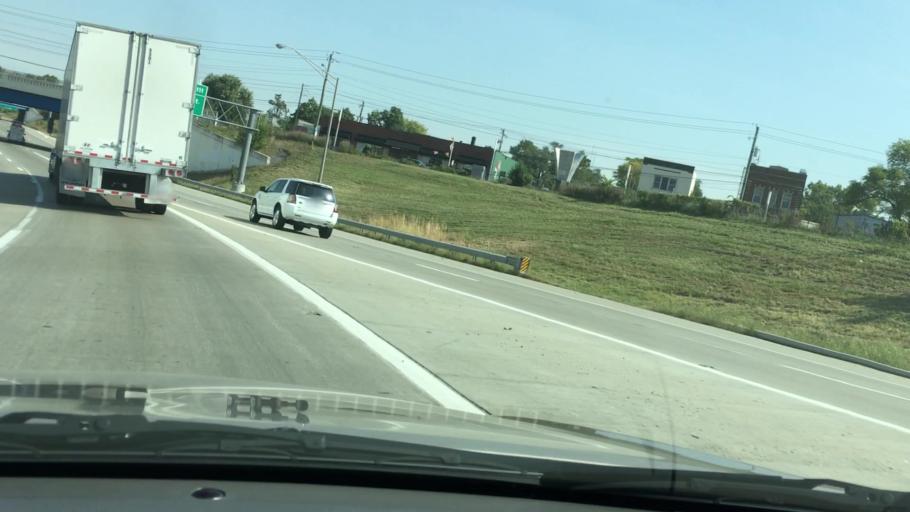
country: US
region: Indiana
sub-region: Marion County
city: Indianapolis
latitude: 39.7546
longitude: -86.1438
